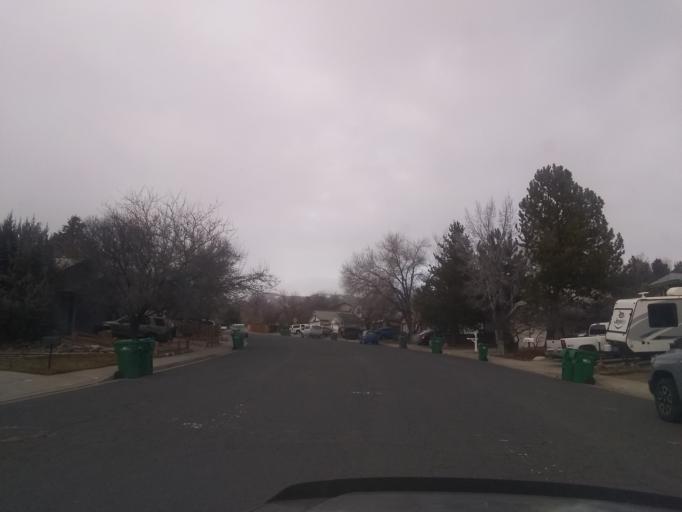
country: US
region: Nevada
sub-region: Washoe County
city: Mogul
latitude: 39.5238
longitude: -119.8845
